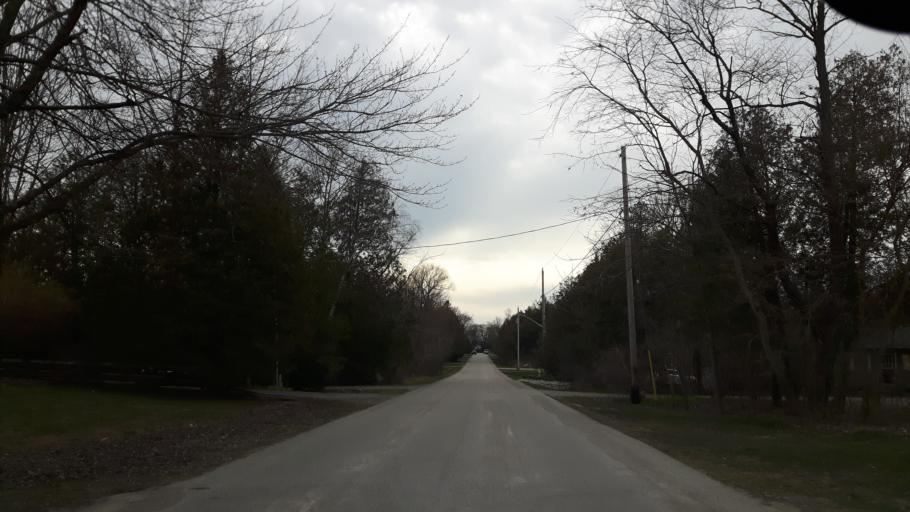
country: CA
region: Ontario
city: Bluewater
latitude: 43.5605
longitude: -81.6993
